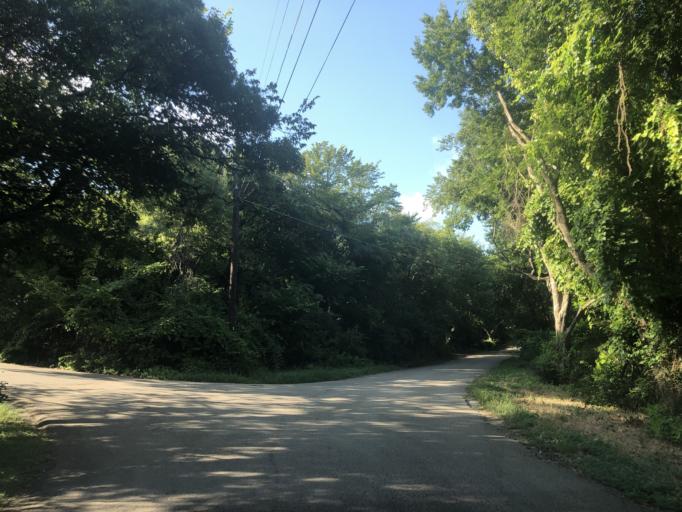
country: US
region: Texas
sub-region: Dallas County
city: Duncanville
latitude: 32.6669
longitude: -96.9219
